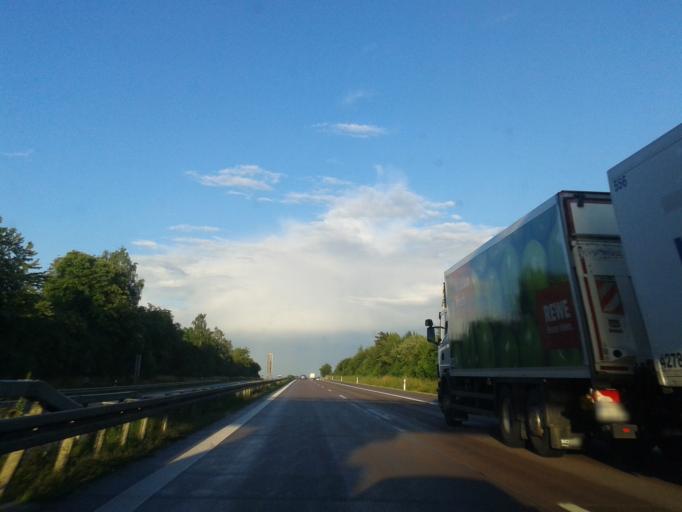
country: DE
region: Saxony
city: Ostrau
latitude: 51.2207
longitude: 12.9212
